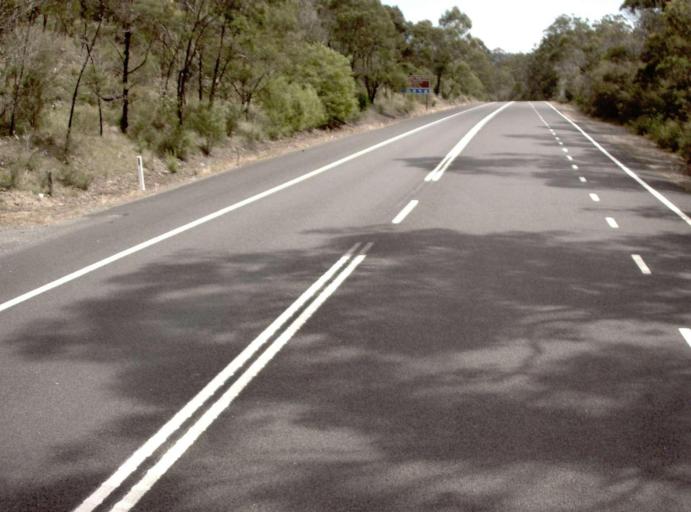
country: AU
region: New South Wales
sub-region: Bega Valley
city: Eden
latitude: -37.4601
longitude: 149.5904
